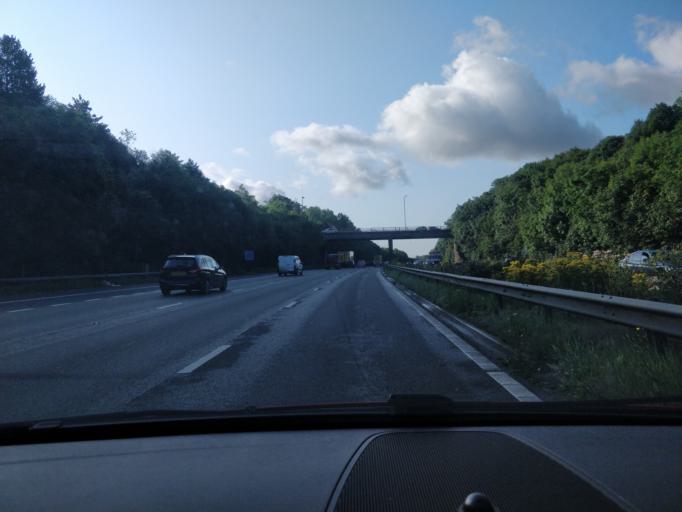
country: GB
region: England
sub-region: Knowsley
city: Prescot
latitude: 53.4270
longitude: -2.8197
